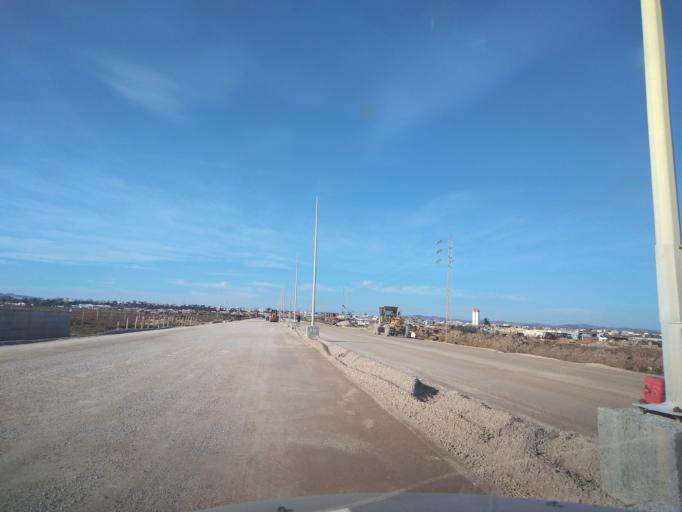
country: TN
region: Ariana
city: Qal'at al Andalus
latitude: 37.0429
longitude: 10.1289
